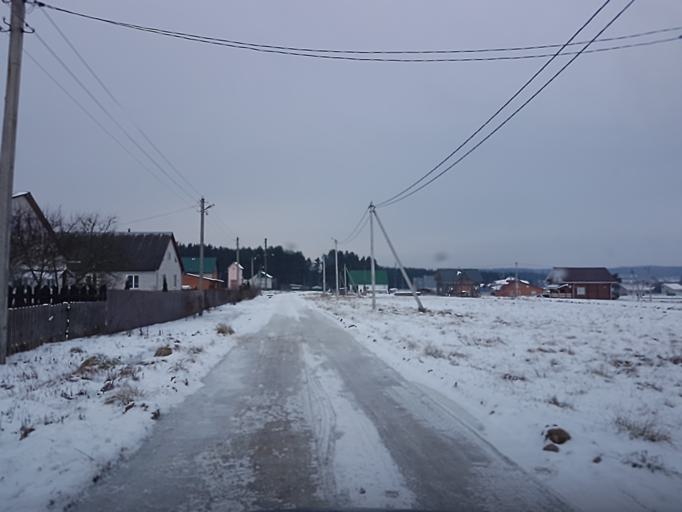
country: BY
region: Minsk
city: Rakaw
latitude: 53.9628
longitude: 27.0391
